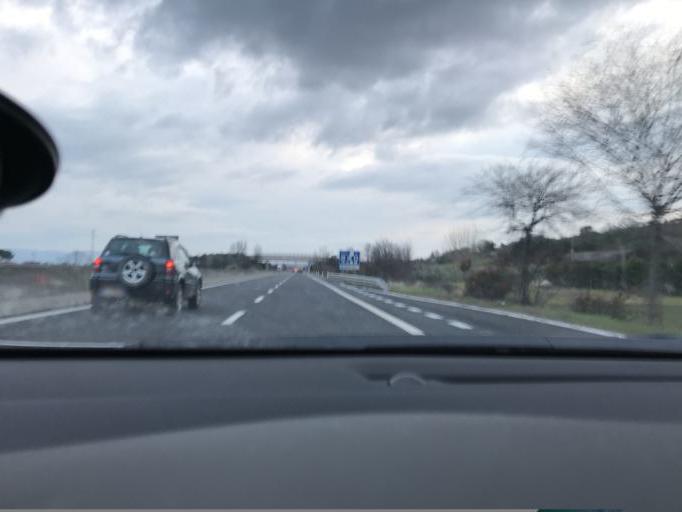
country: IT
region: Umbria
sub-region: Provincia di Perugia
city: Petrignano
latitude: 43.1301
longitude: 12.5209
